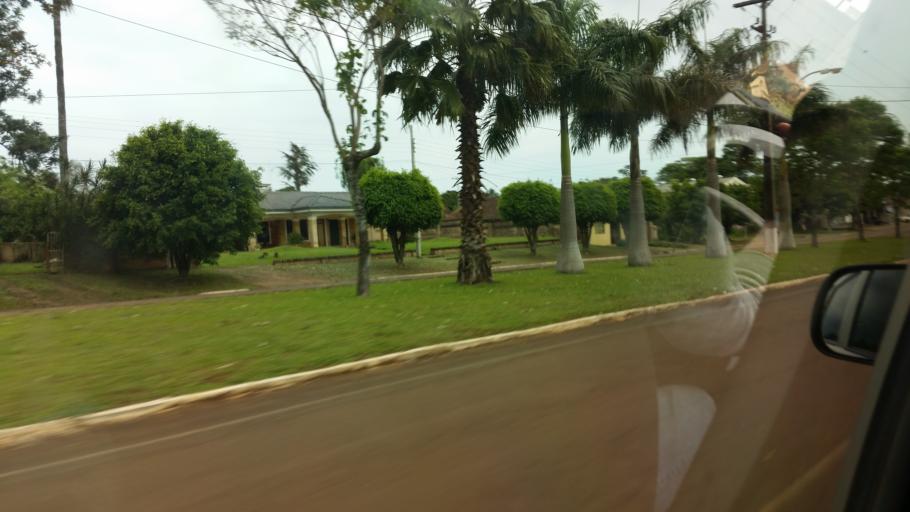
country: PY
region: Itapua
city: Fram
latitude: -27.0962
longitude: -56.0144
